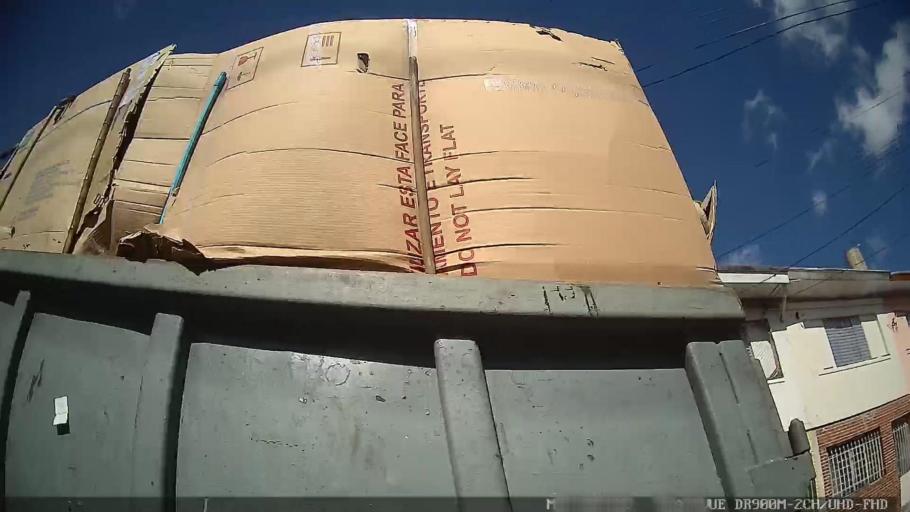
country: BR
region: Sao Paulo
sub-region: Sao Caetano Do Sul
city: Sao Caetano do Sul
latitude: -23.6090
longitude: -46.5978
